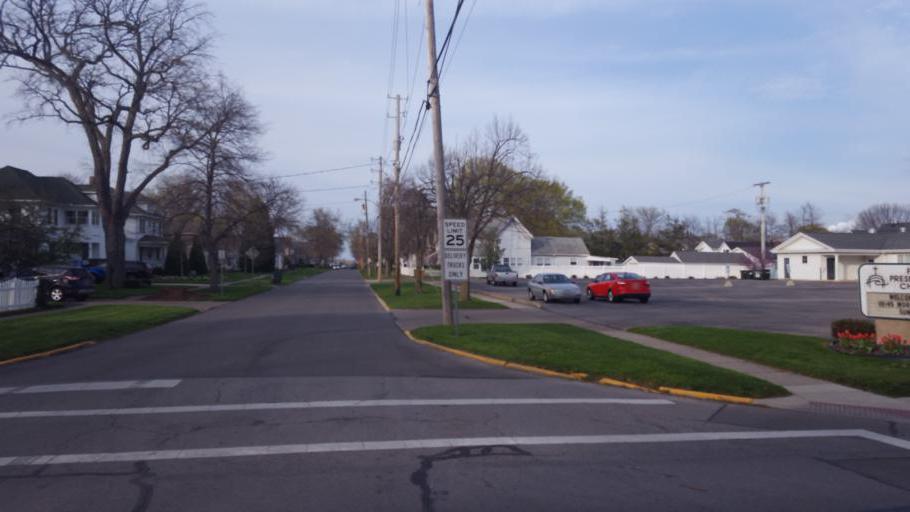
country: US
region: Ohio
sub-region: Erie County
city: Huron
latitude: 41.3956
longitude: -82.5565
